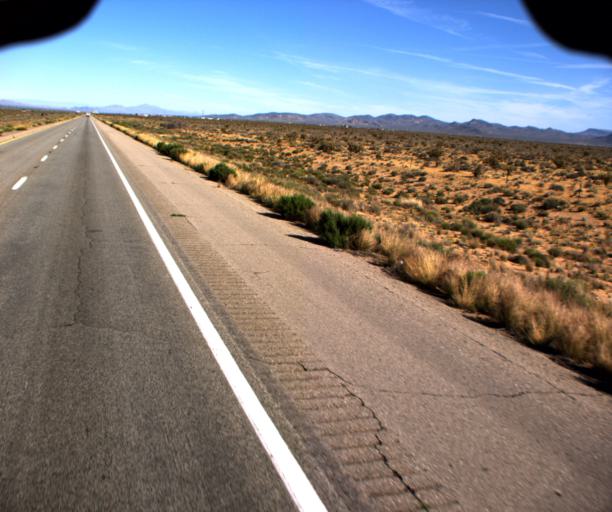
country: US
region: Arizona
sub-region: Mohave County
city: Dolan Springs
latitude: 35.5042
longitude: -114.3346
